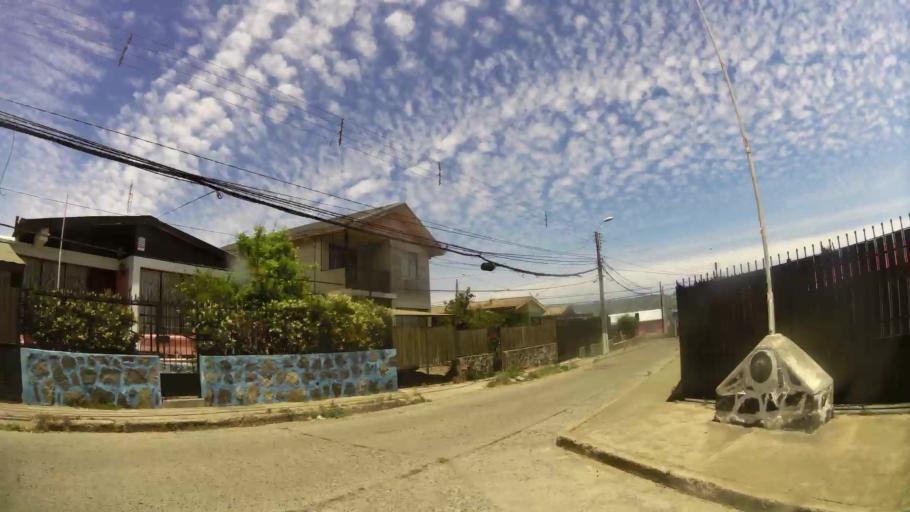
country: CL
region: Valparaiso
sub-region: Provincia de Valparaiso
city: Vina del Mar
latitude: -33.0489
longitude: -71.5793
